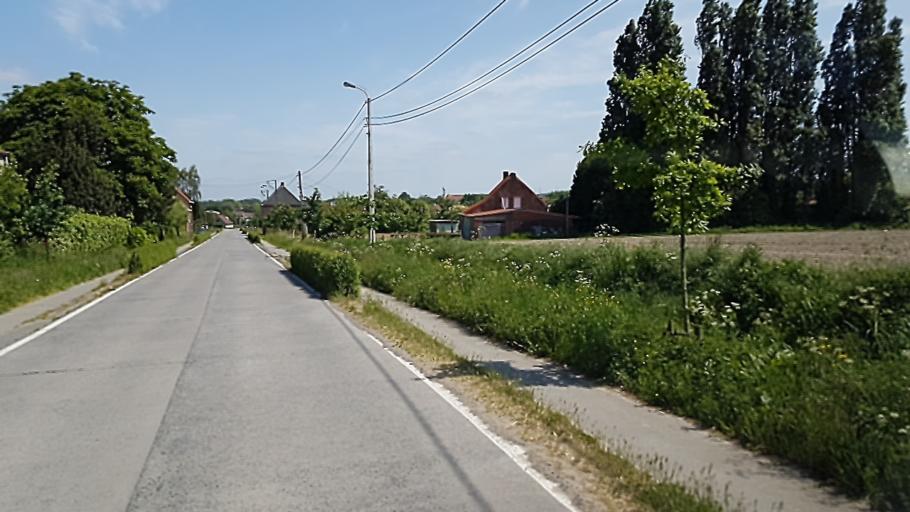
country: BE
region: Flanders
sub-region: Provincie West-Vlaanderen
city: Anzegem
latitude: 50.8343
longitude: 3.4642
